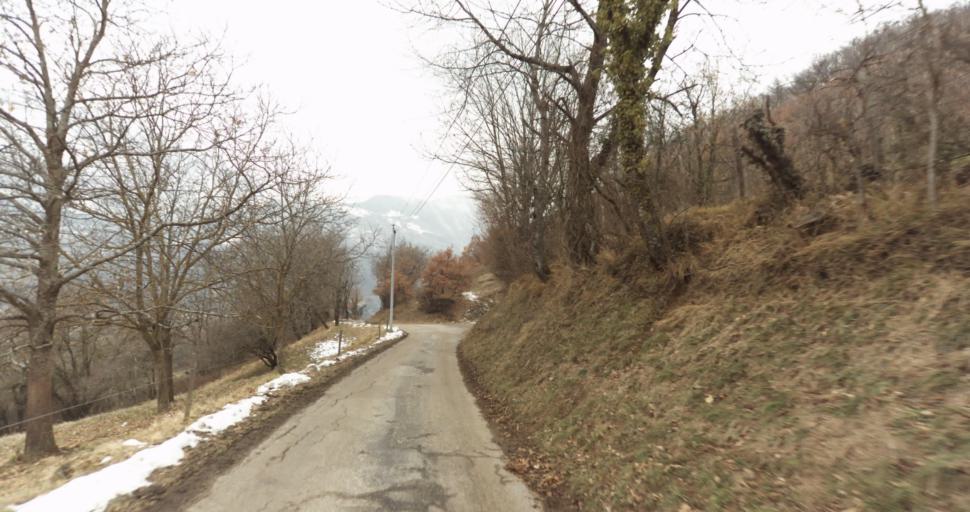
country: FR
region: Rhone-Alpes
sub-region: Departement de l'Isere
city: Vif
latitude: 45.0191
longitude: 5.6652
